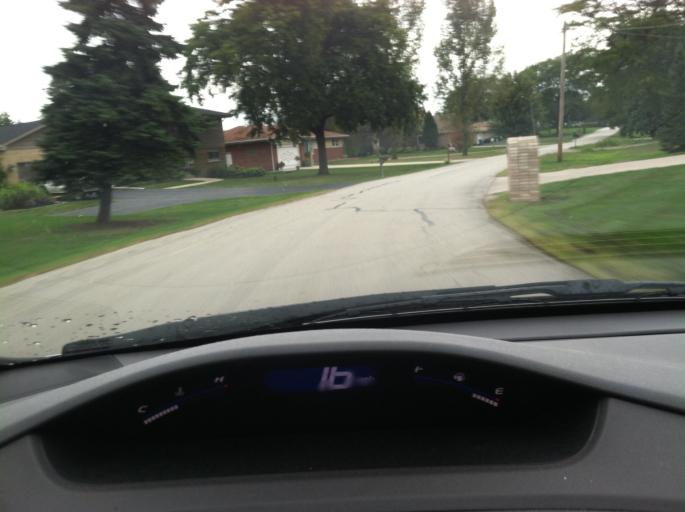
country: US
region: Illinois
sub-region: DuPage County
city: Wood Dale
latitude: 41.9748
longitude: -87.9630
